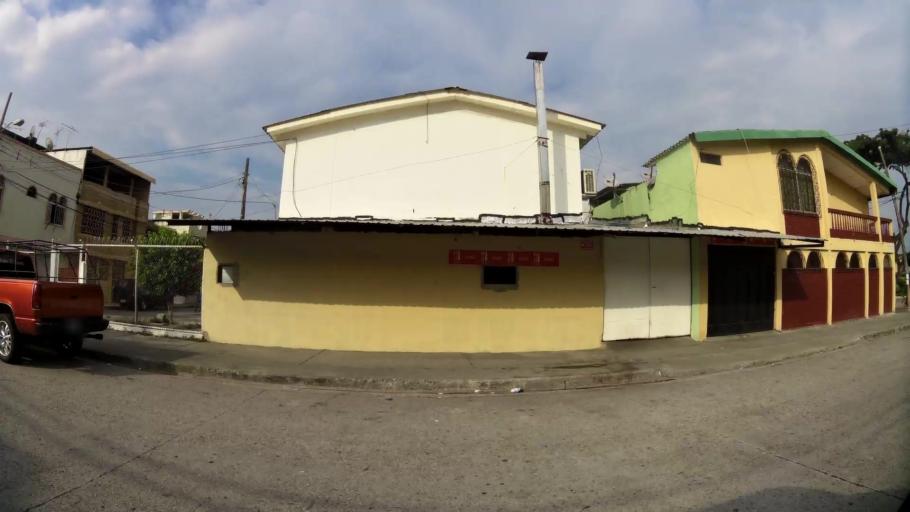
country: EC
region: Guayas
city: Guayaquil
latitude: -2.2441
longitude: -79.9015
